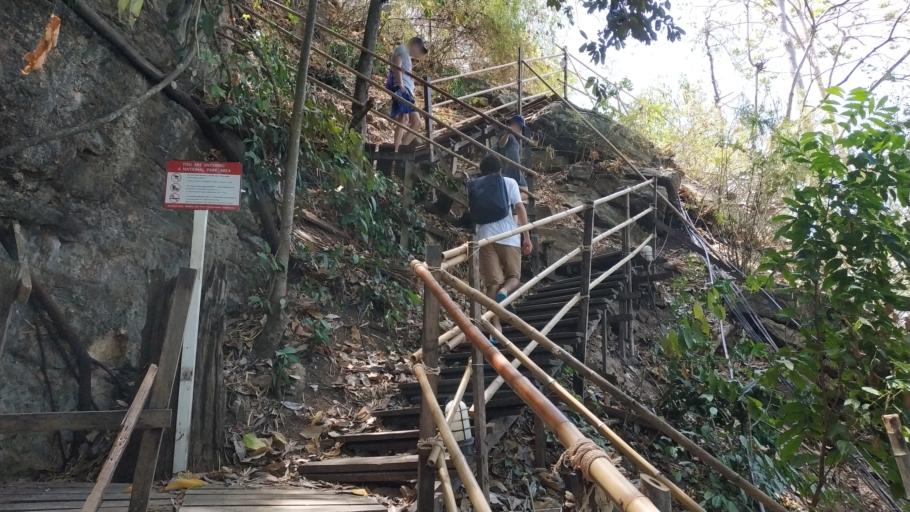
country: TH
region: Phangnga
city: Ban Ao Nang
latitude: 8.0262
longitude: 98.8271
